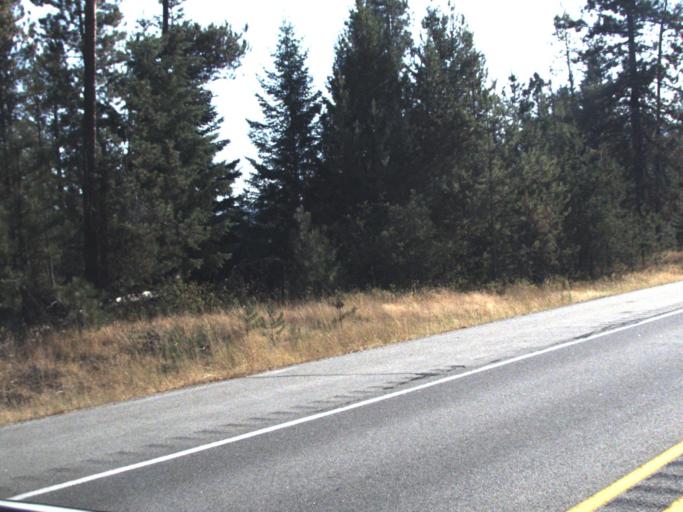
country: US
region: Washington
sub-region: Pend Oreille County
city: Newport
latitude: 48.1550
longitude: -117.1009
